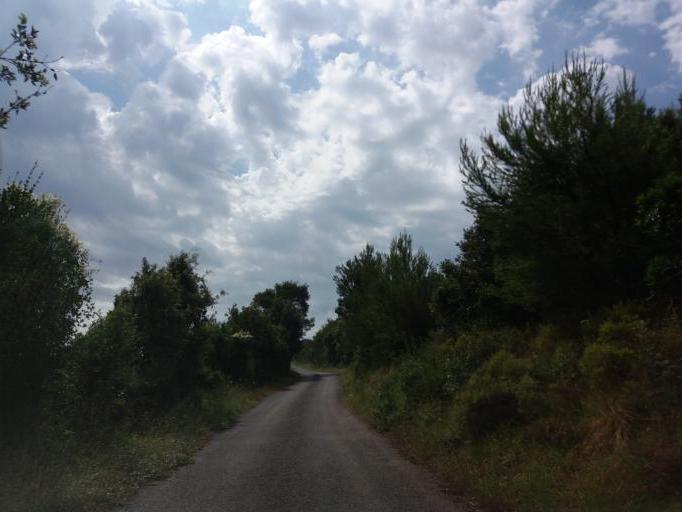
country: HR
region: Zadarska
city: Sali
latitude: 43.9093
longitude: 15.1296
